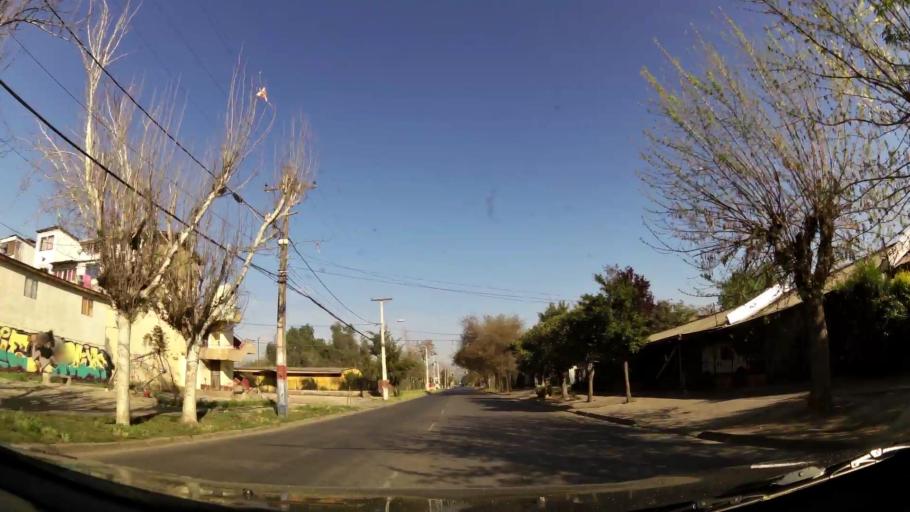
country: CL
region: Santiago Metropolitan
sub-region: Provincia de Santiago
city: Santiago
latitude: -33.3845
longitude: -70.6558
